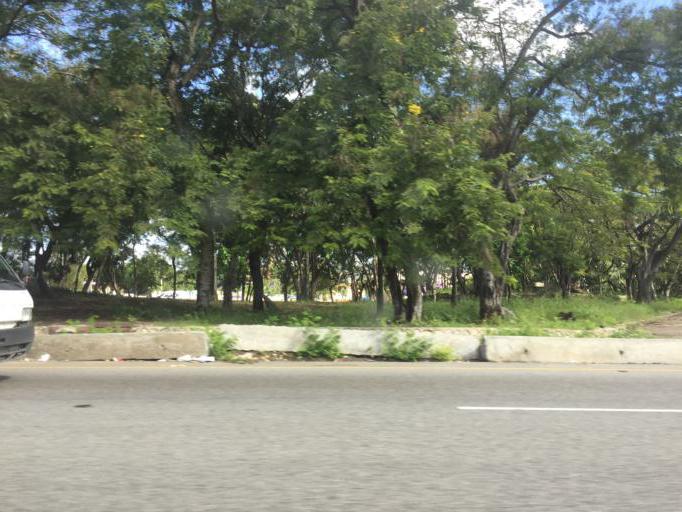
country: DO
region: Santo Domingo
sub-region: Santo Domingo
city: Santo Domingo Este
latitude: 18.4846
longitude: -69.8512
